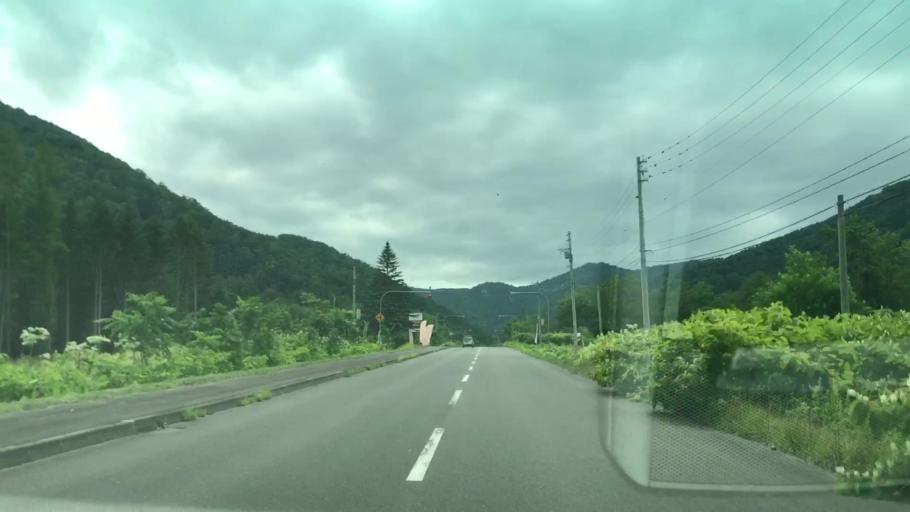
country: JP
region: Hokkaido
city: Yoichi
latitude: 43.0290
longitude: 140.8659
